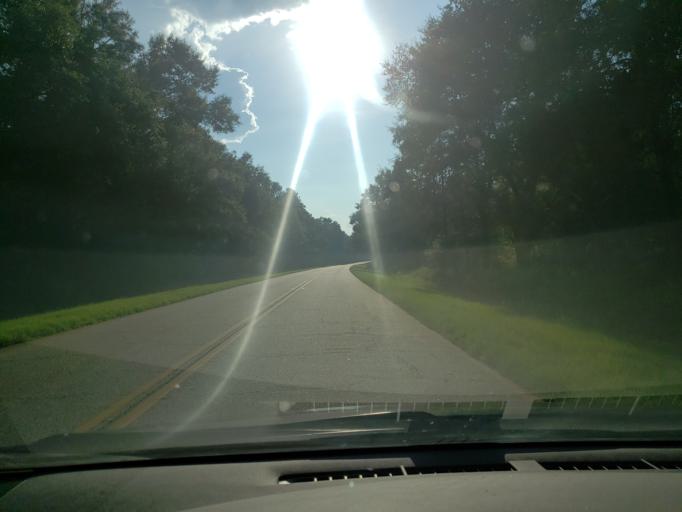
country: US
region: Georgia
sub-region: Dougherty County
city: Albany
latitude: 31.5728
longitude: -84.3315
